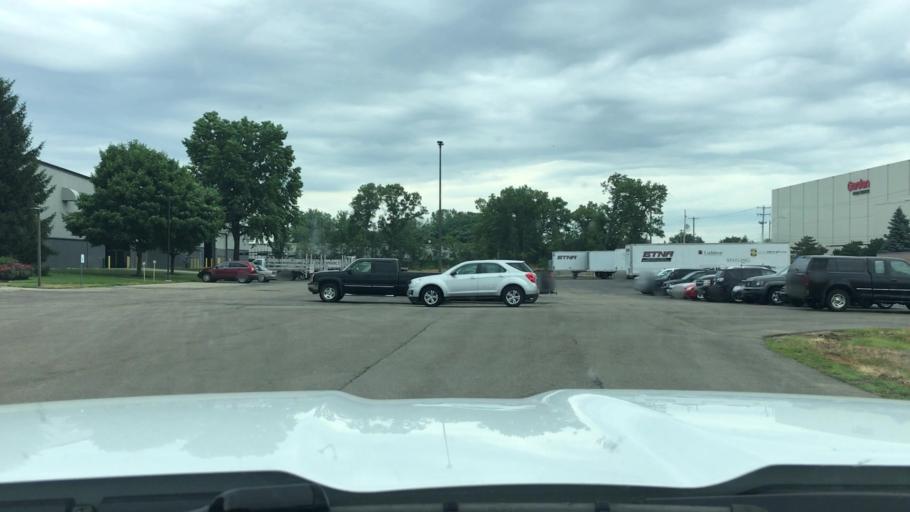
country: US
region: Michigan
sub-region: Kent County
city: Kentwood
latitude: 42.8748
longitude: -85.6784
